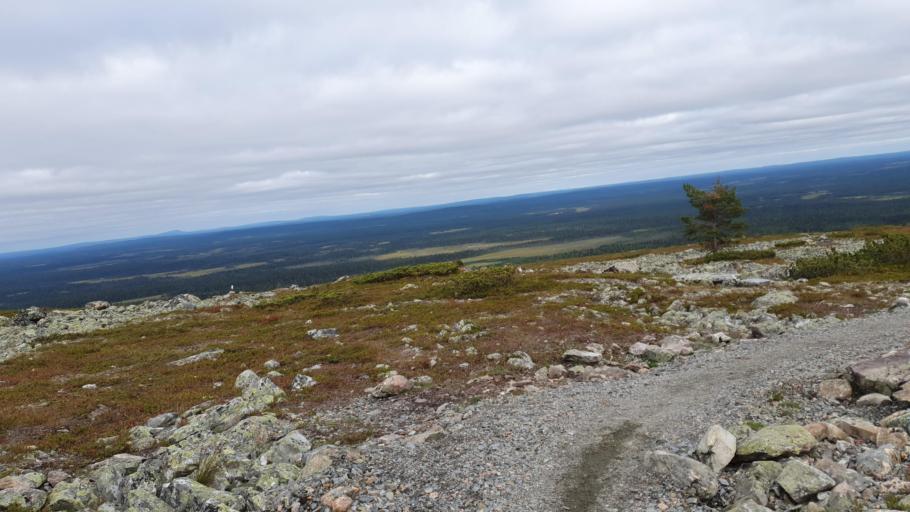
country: FI
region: Lapland
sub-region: Tunturi-Lappi
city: Kolari
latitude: 67.5673
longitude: 24.2470
